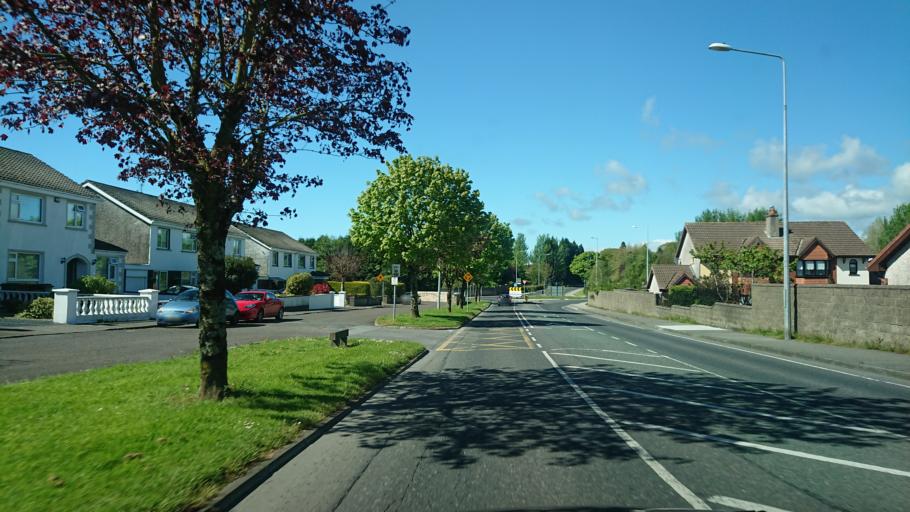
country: IE
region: Munster
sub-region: Waterford
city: Waterford
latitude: 52.2552
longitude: -7.1440
